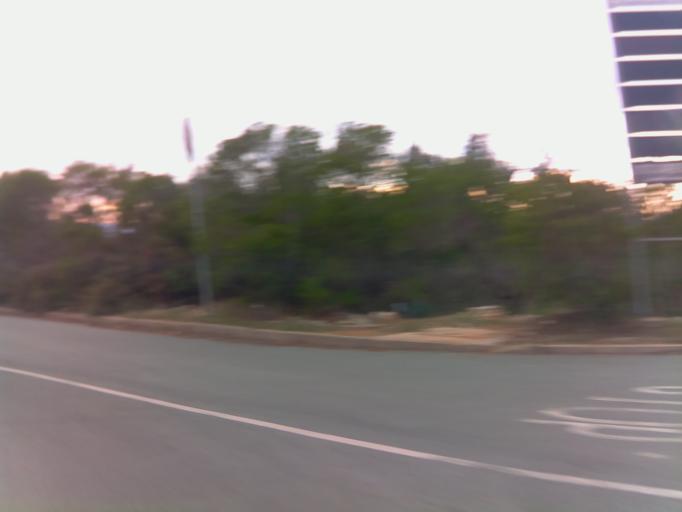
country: CY
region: Pafos
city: Pegeia
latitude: 34.8860
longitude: 32.3378
